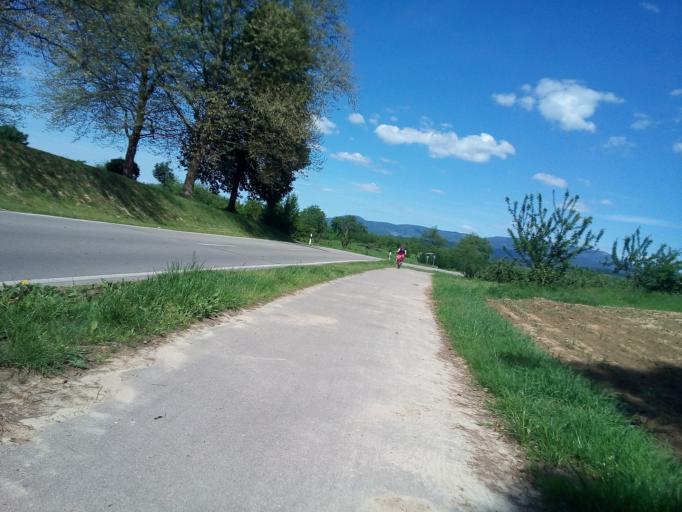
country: DE
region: Baden-Wuerttemberg
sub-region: Freiburg Region
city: Renchen
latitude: 48.5700
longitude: 8.0268
